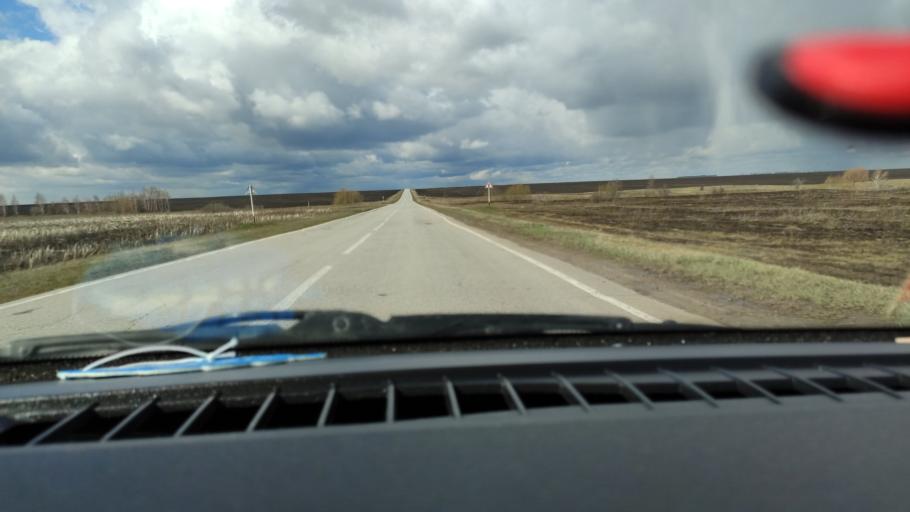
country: RU
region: Samara
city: Novyy Buyan
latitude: 53.7866
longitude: 50.0781
